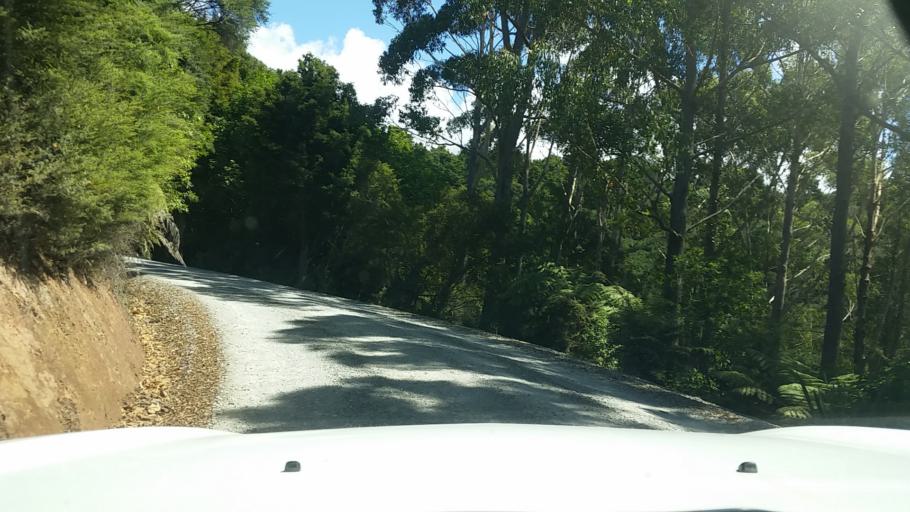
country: NZ
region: Northland
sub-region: Whangarei
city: Ngunguru
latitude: -35.6124
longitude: 174.4865
